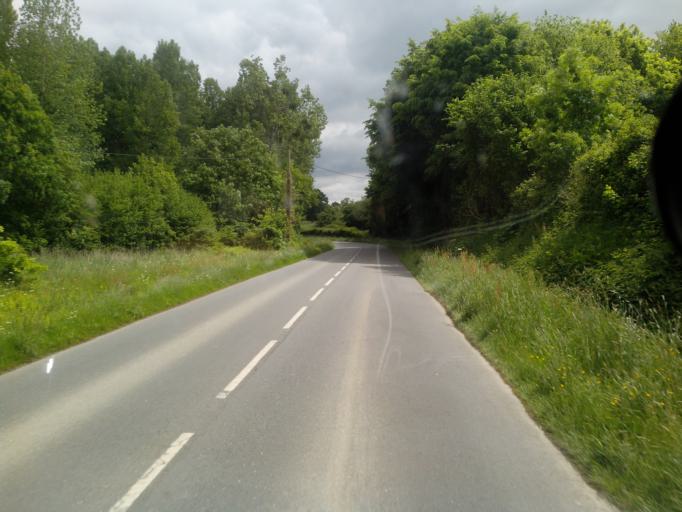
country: FR
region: Brittany
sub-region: Departement d'Ille-et-Vilaine
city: Chasne-sur-Illet
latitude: 48.2455
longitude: -1.5705
